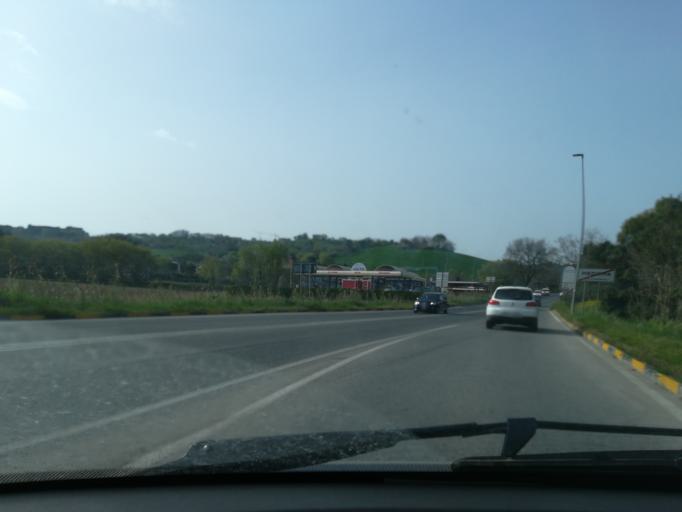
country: IT
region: The Marches
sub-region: Provincia di Macerata
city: Piediripa
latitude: 43.2815
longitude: 13.4851
